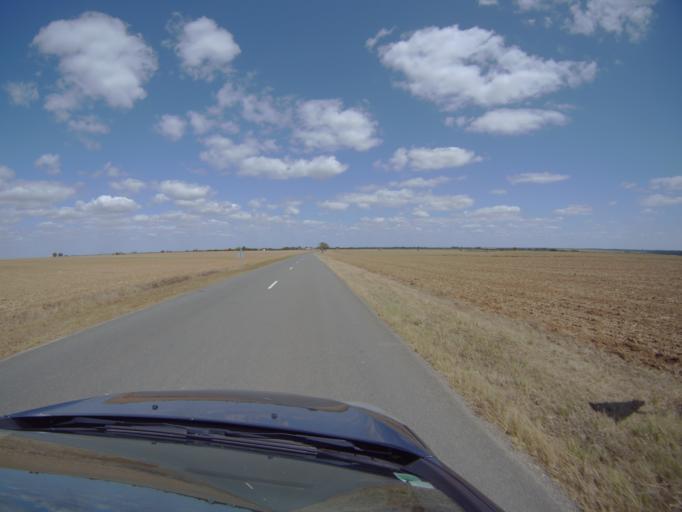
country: FR
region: Poitou-Charentes
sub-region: Departement des Deux-Sevres
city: Saint-Hilaire-la-Palud
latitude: 46.2664
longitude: -0.6734
